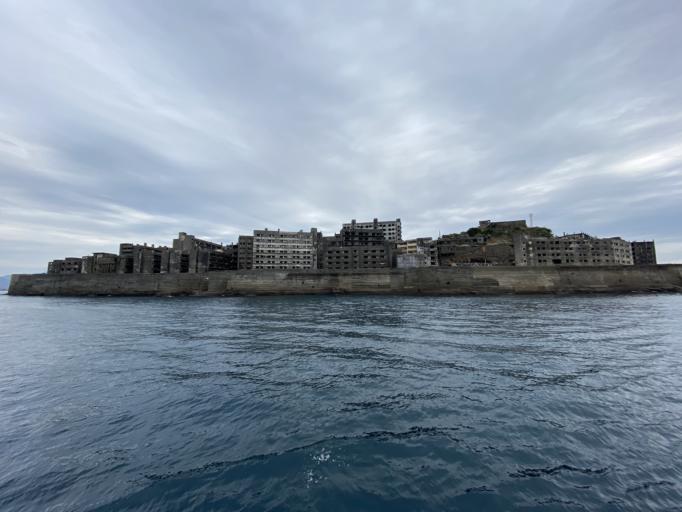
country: JP
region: Nagasaki
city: Nagasaki-shi
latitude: 32.6287
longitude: 129.7365
